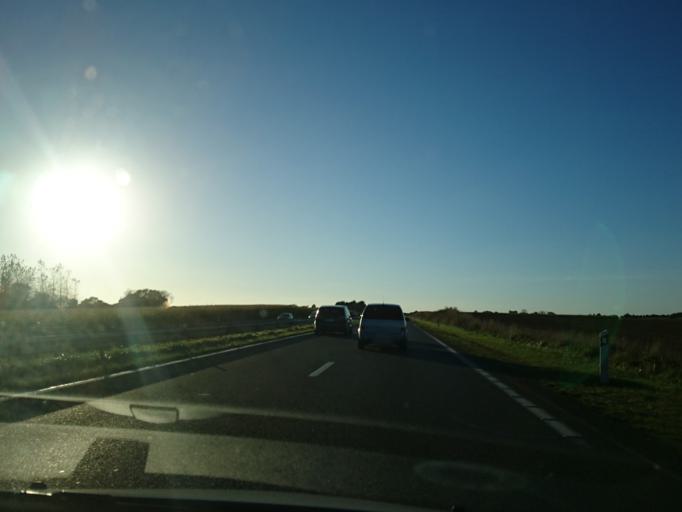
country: FR
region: Brittany
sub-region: Departement des Cotes-d'Armor
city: Pordic
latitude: 48.5451
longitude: -2.8103
